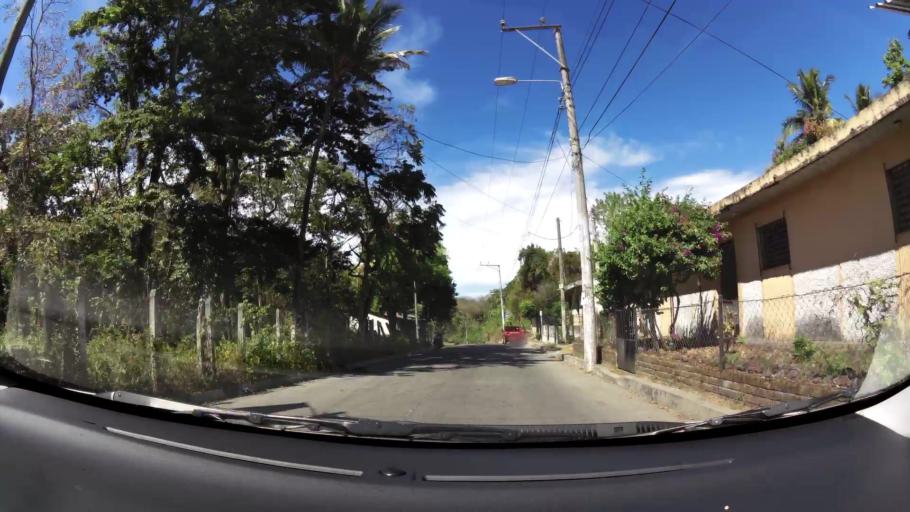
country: SV
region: San Salvador
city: Apopa
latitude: 13.8101
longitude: -89.1736
